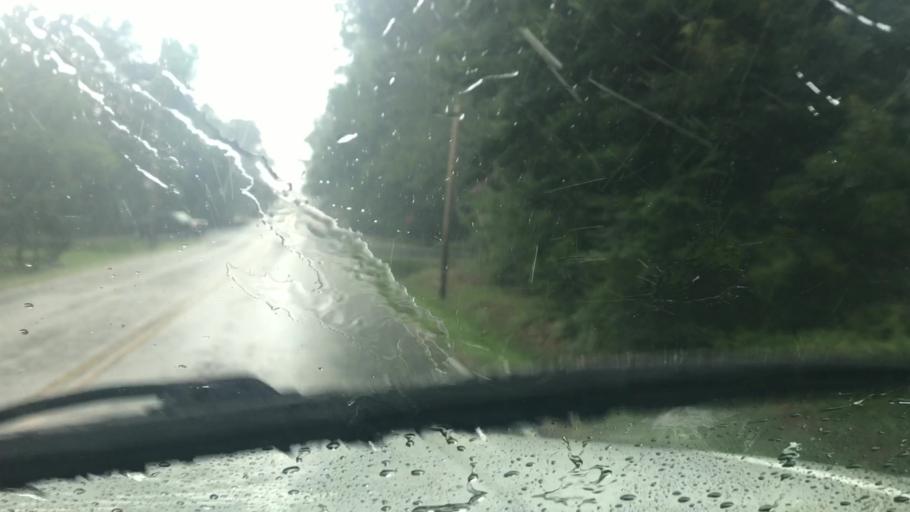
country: US
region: Virginia
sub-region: Henrico County
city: Tuckahoe
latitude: 37.5991
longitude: -77.5376
